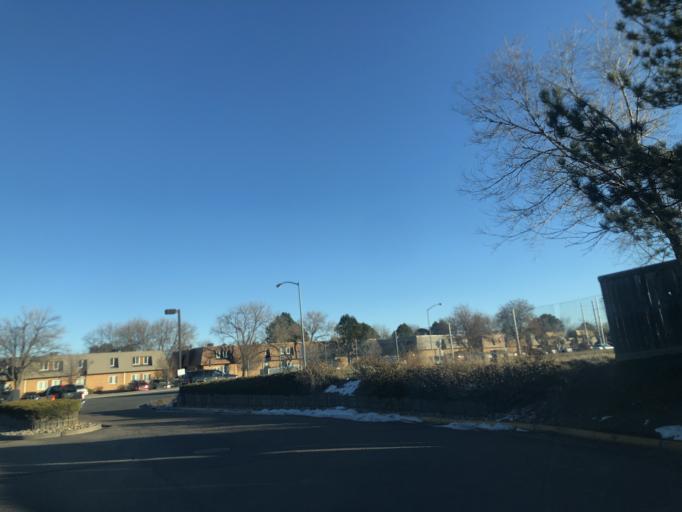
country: US
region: Colorado
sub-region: Adams County
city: Aurora
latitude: 39.7178
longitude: -104.8201
